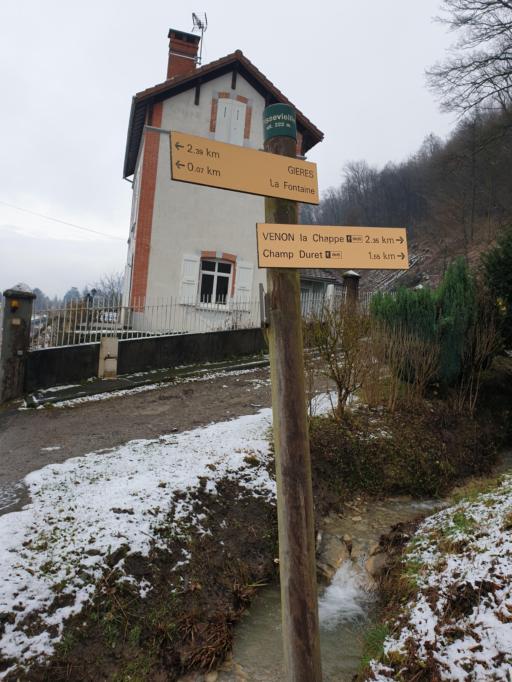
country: FR
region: Rhone-Alpes
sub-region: Departement de l'Isere
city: Gieres
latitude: 45.1874
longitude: 5.8121
